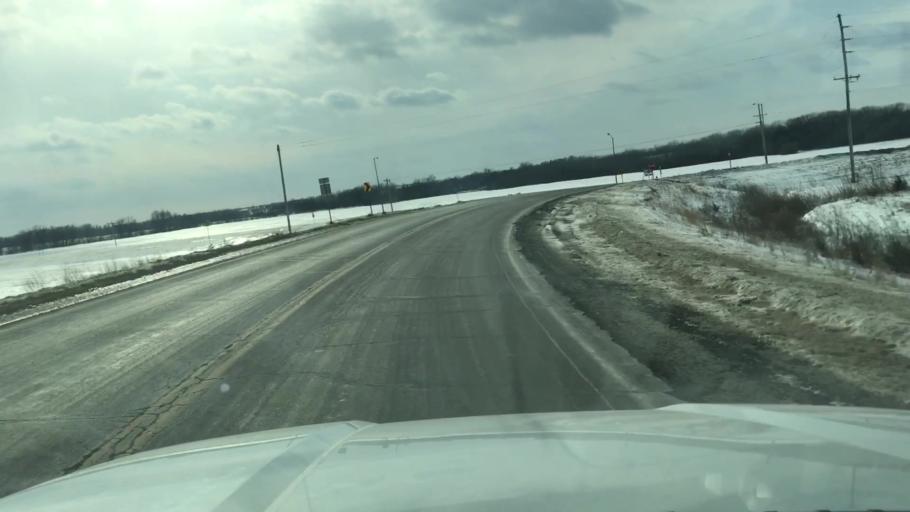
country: US
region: Missouri
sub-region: Gentry County
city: Stanberry
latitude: 40.3420
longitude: -94.6750
